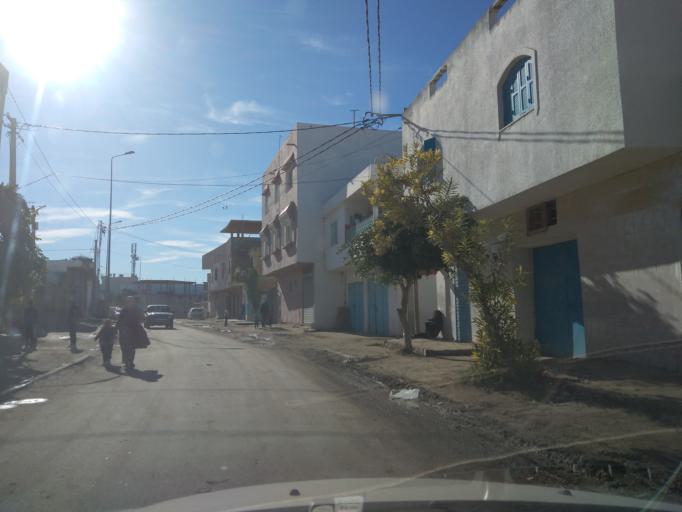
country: TN
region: Ariana
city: Qal'at al Andalus
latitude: 37.0668
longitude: 10.1215
